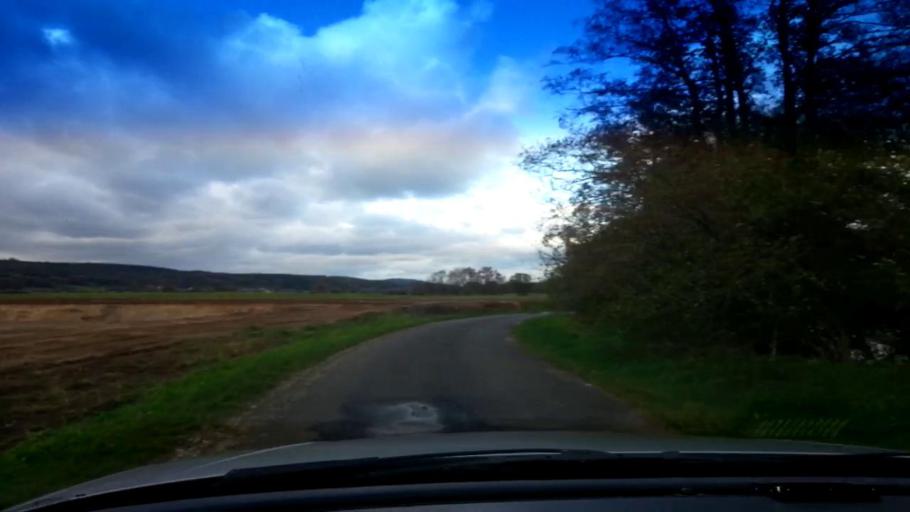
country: DE
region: Bavaria
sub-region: Upper Franconia
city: Zapfendorf
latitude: 50.0297
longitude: 10.9308
